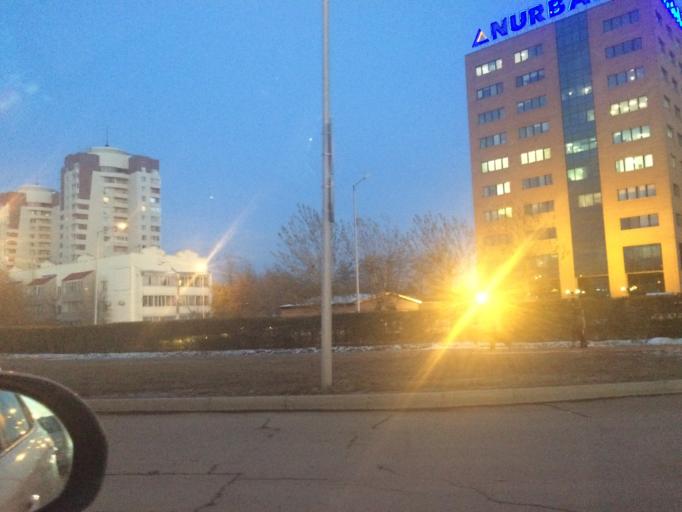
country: KZ
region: Astana Qalasy
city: Astana
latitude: 51.1477
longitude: 71.4231
